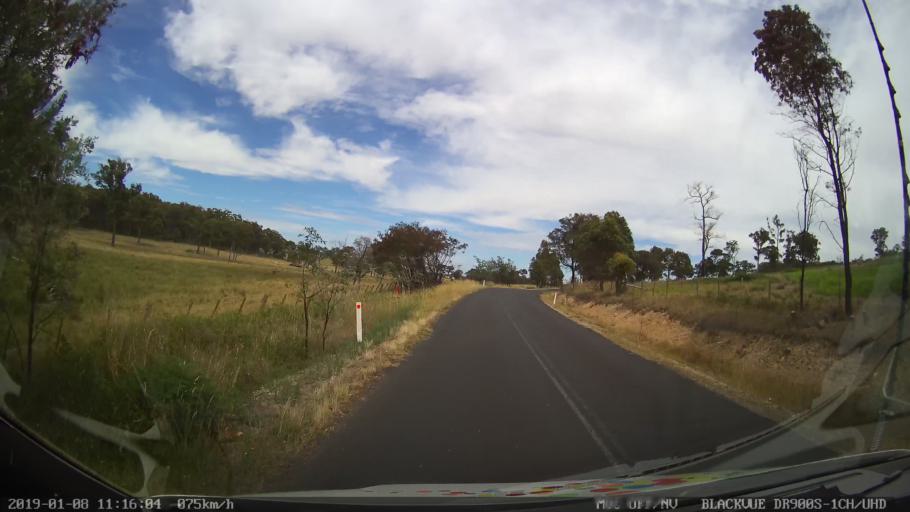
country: AU
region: New South Wales
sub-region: Guyra
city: Guyra
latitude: -30.2219
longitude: 151.5690
